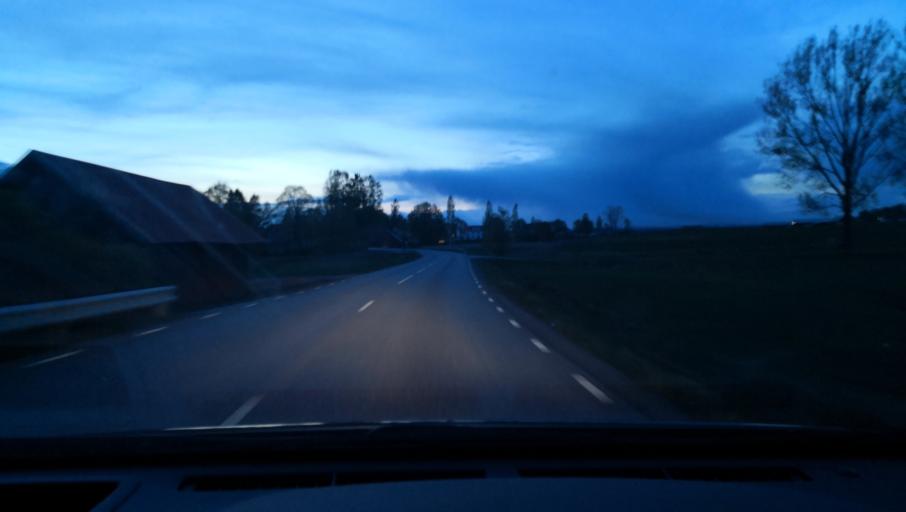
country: SE
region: OErebro
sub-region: Hallsbergs Kommun
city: Hallsberg
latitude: 59.1247
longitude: 14.9942
